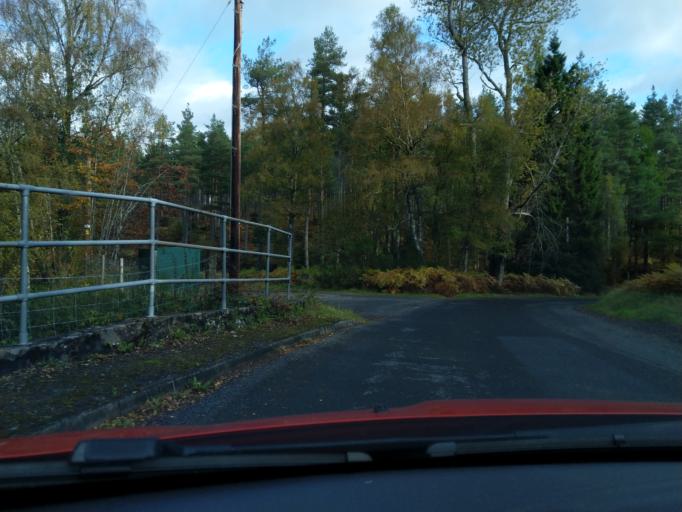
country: GB
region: Scotland
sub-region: Perth and Kinross
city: Aberfeldy
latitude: 56.7087
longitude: -4.0716
